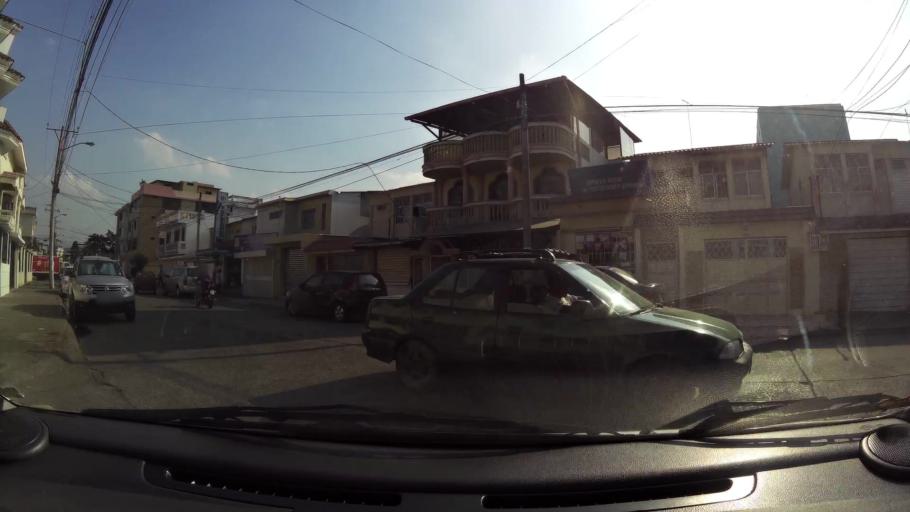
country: EC
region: Guayas
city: Guayaquil
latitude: -2.1491
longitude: -79.9090
